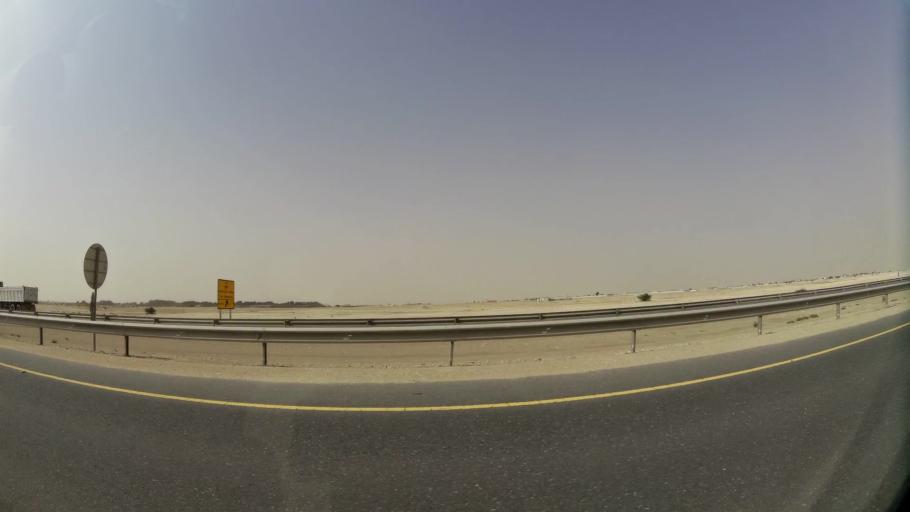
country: QA
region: Baladiyat ar Rayyan
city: Ar Rayyan
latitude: 25.1592
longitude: 51.2906
